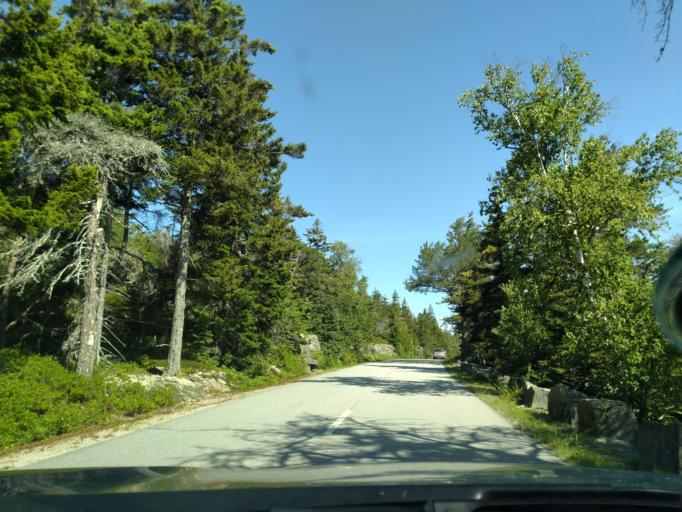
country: US
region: Maine
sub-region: Hancock County
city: Gouldsboro
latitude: 44.3509
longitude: -68.0466
